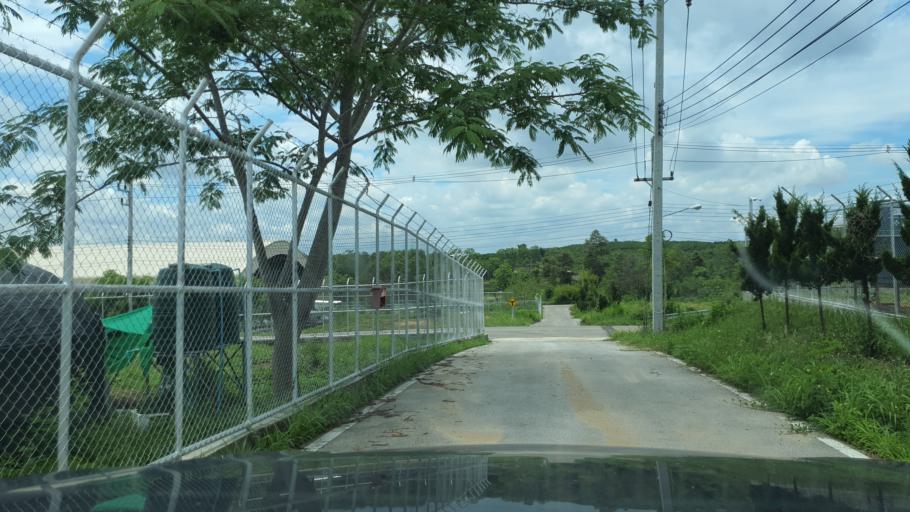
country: TH
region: Chiang Mai
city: San Sai
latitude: 18.9255
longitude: 99.0548
